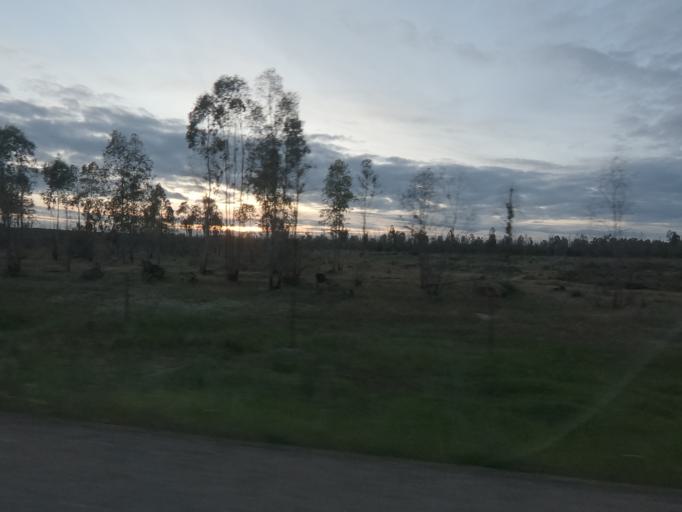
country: ES
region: Extremadura
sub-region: Provincia de Badajoz
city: Badajoz
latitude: 38.9852
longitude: -6.8800
